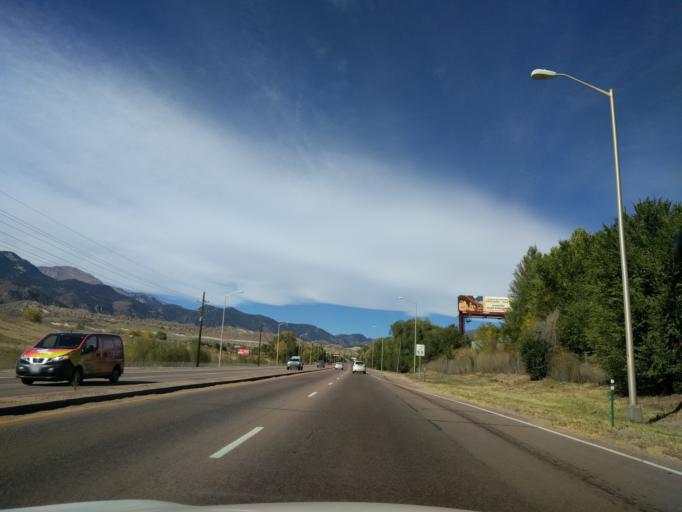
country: US
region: Colorado
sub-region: El Paso County
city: Colorado Springs
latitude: 38.8365
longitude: -104.8511
